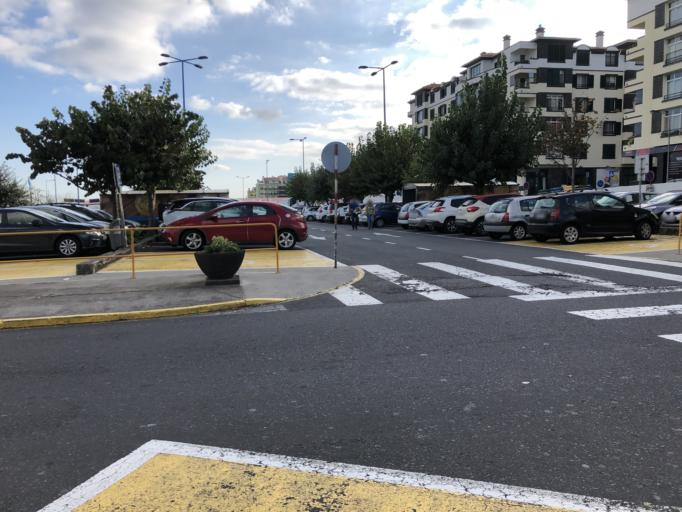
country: PT
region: Azores
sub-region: Ponta Delgada
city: Rosto de Cao
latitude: 37.7521
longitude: -25.6571
